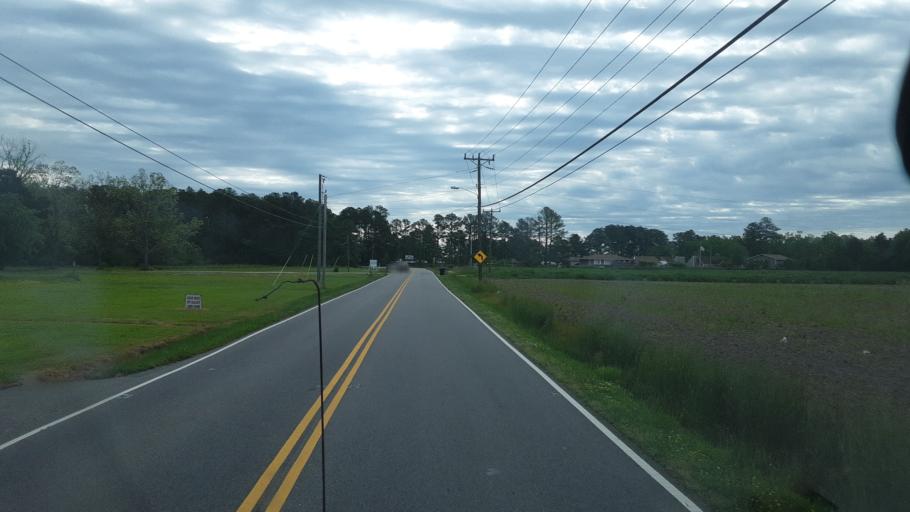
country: US
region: Virginia
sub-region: City of Virginia Beach
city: Virginia Beach
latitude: 36.7308
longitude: -75.9764
